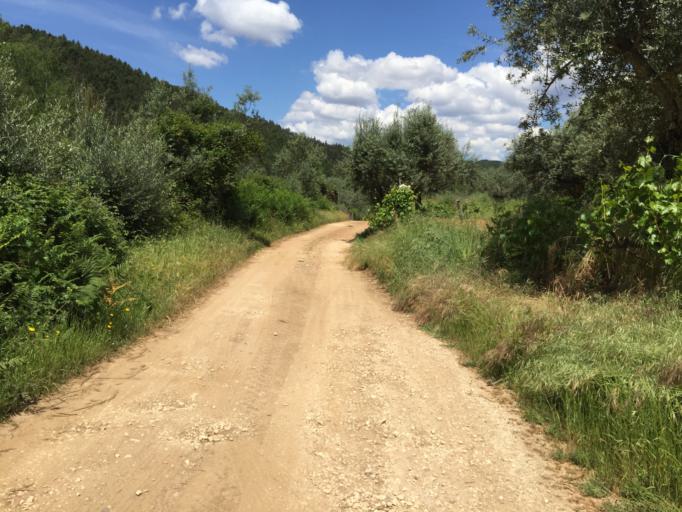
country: PT
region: Coimbra
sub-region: Pampilhosa da Serra
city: Pampilhosa da Serra
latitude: 40.0748
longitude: -7.7852
